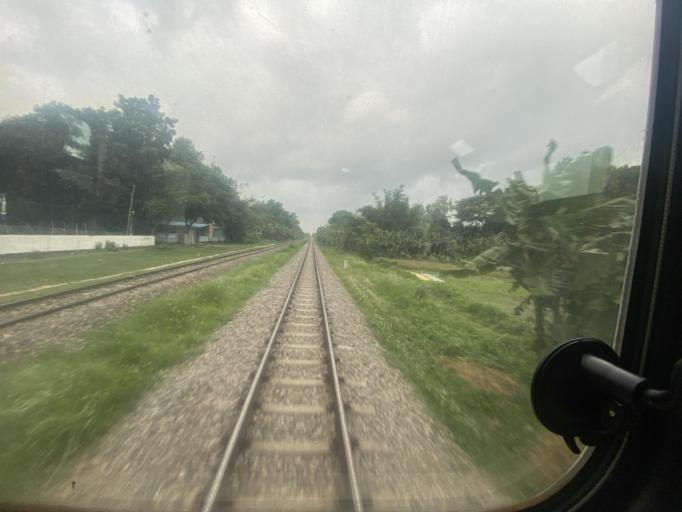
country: BD
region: Dhaka
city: Narsingdi
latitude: 23.9308
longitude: 90.6891
